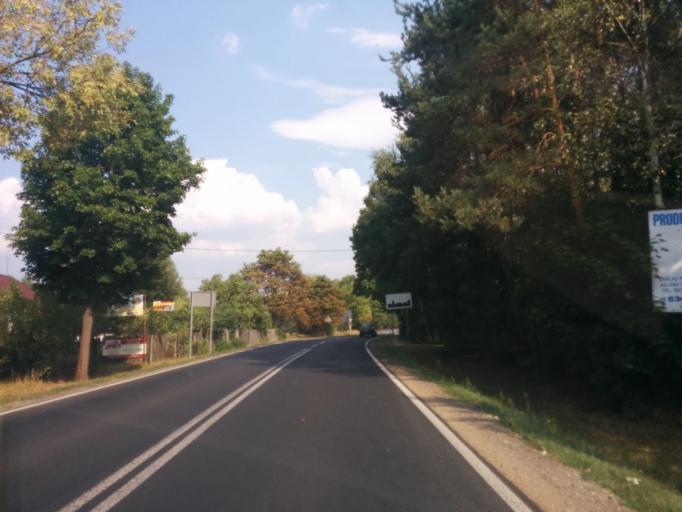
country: PL
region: Silesian Voivodeship
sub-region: Powiat myszkowski
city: Zarki-Letnisko
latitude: 50.6045
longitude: 19.2752
